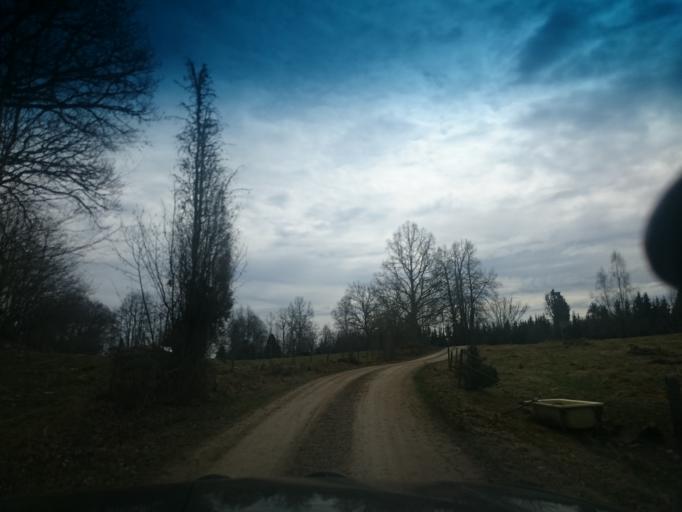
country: SE
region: Joenkoeping
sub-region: Vetlanda Kommun
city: Vetlanda
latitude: 57.3260
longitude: 15.1858
